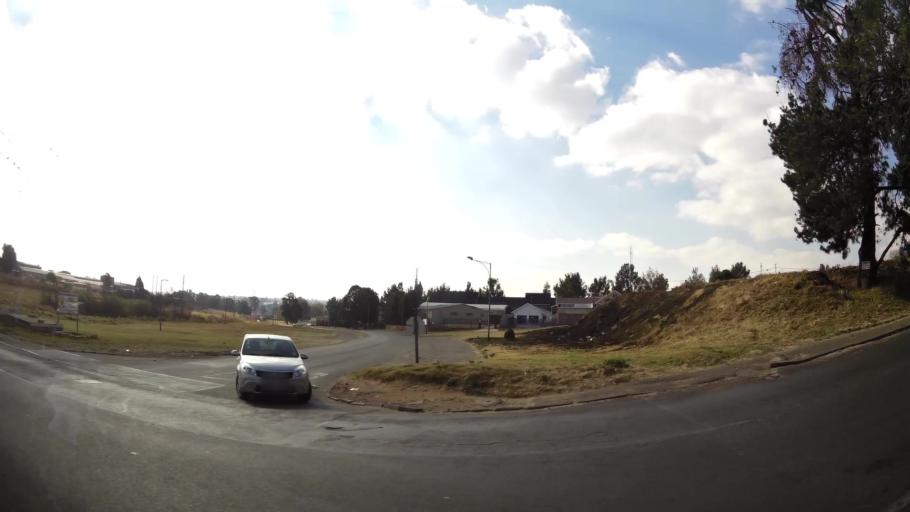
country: ZA
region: Gauteng
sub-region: West Rand District Municipality
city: Krugersdorp
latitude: -26.1049
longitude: 27.7660
